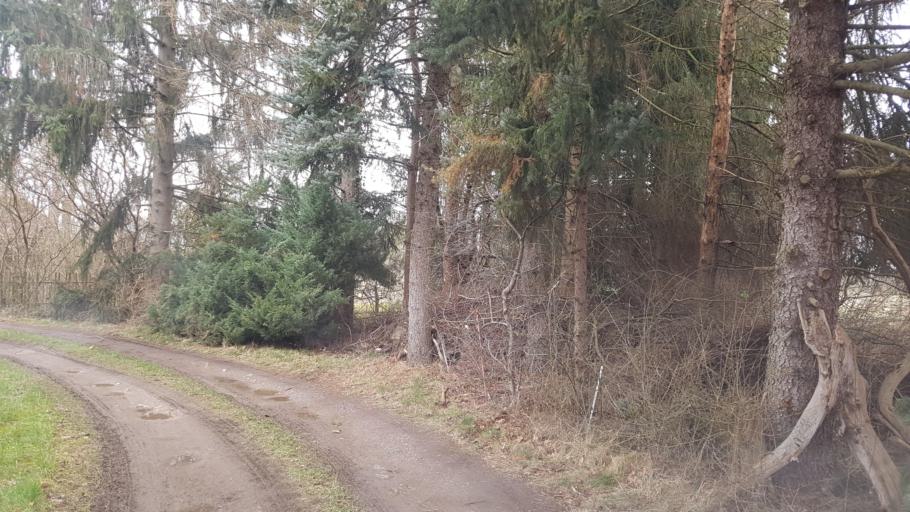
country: DE
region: Brandenburg
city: Kroppen
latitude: 51.3832
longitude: 13.7801
